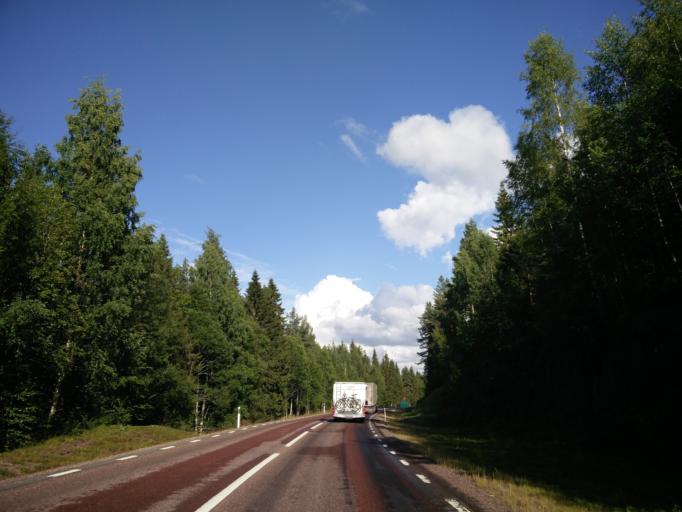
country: SE
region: Vaermland
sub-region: Hagfors Kommun
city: Ekshaerad
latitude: 60.4806
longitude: 13.3176
